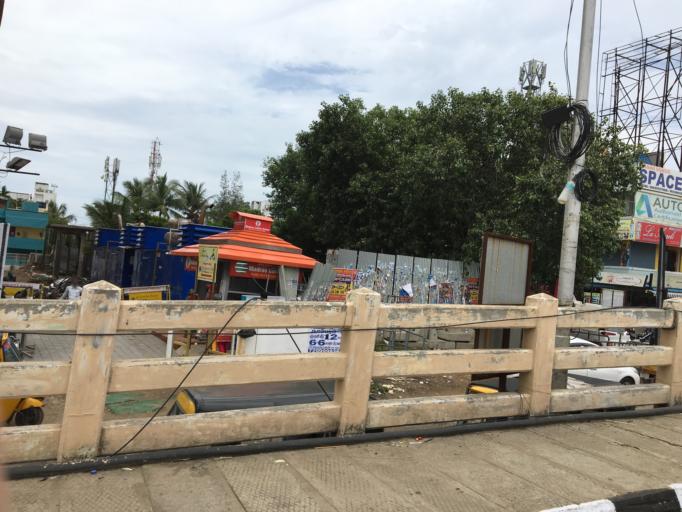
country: IN
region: Tamil Nadu
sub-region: Kancheepuram
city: Madipakkam
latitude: 12.9701
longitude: 80.2188
